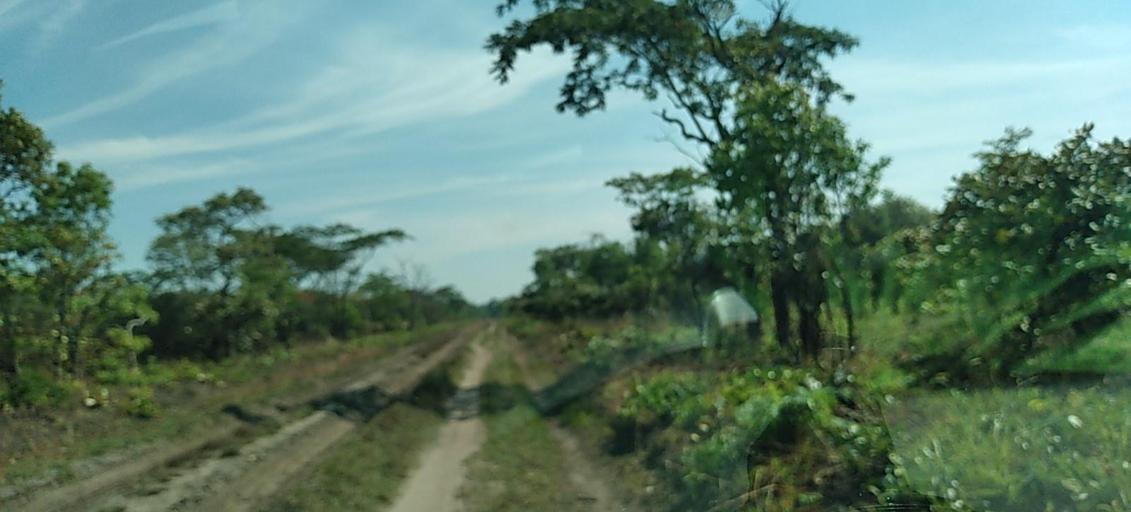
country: ZM
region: North-Western
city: Mwinilunga
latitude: -11.8022
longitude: 25.1658
